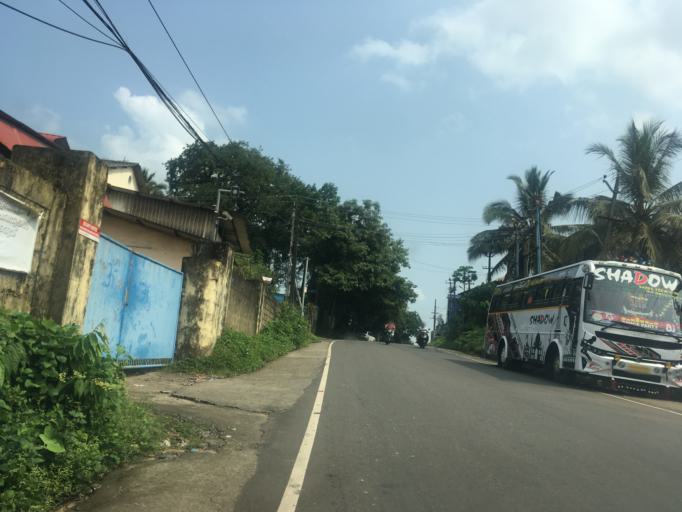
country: IN
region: Kerala
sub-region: Ernakulam
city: Elur
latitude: 10.0487
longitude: 76.3097
